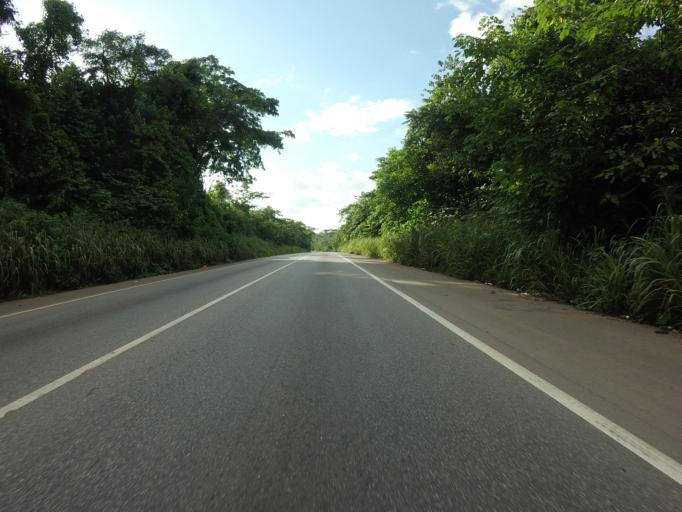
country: GH
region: Ashanti
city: Tafo
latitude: 6.8912
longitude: -1.6487
